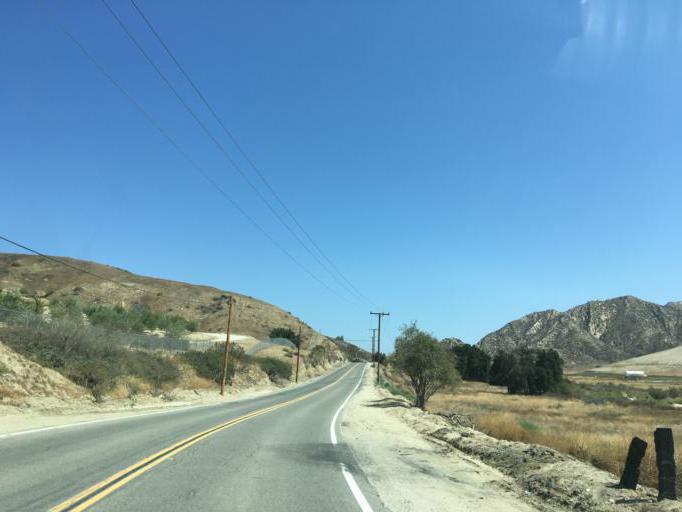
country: US
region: California
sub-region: Los Angeles County
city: Val Verde
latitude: 34.4275
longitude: -118.6587
